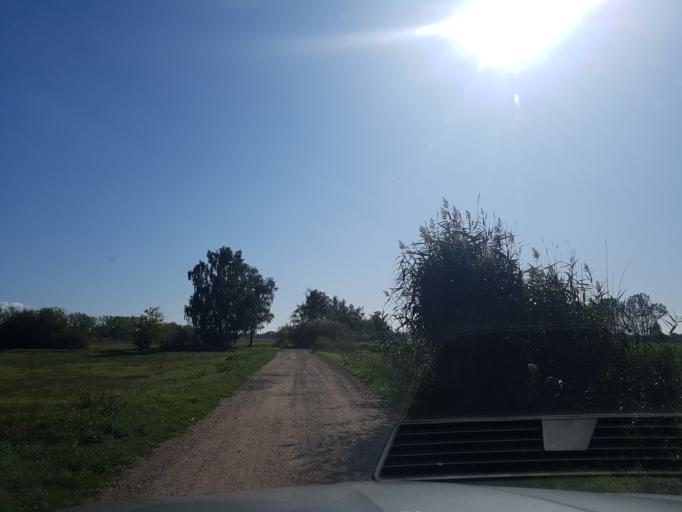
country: DE
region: Brandenburg
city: Bad Liebenwerda
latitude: 51.5427
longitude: 13.3624
